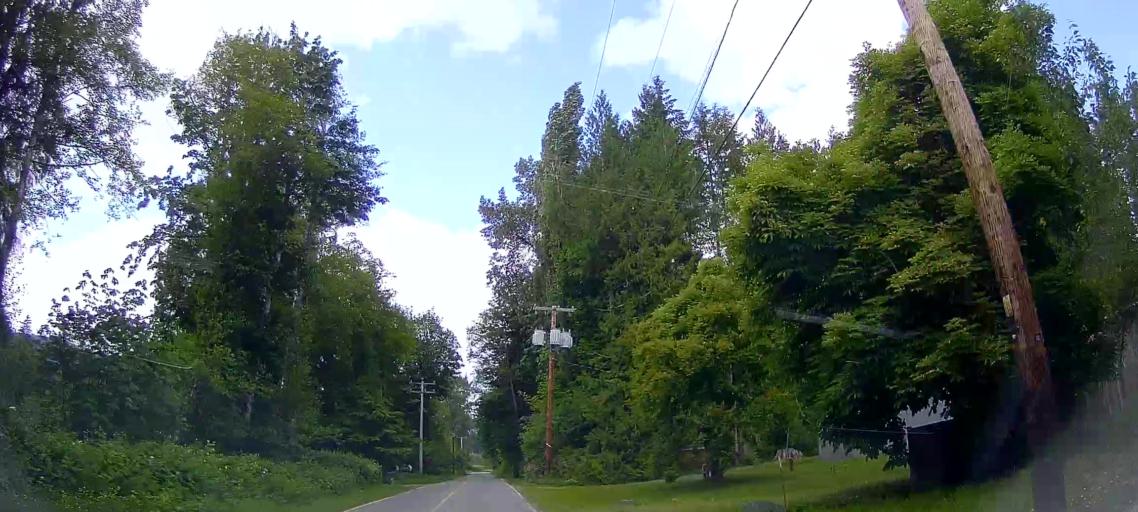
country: US
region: Washington
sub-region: Whatcom County
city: Sudden Valley
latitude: 48.6792
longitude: -122.1694
